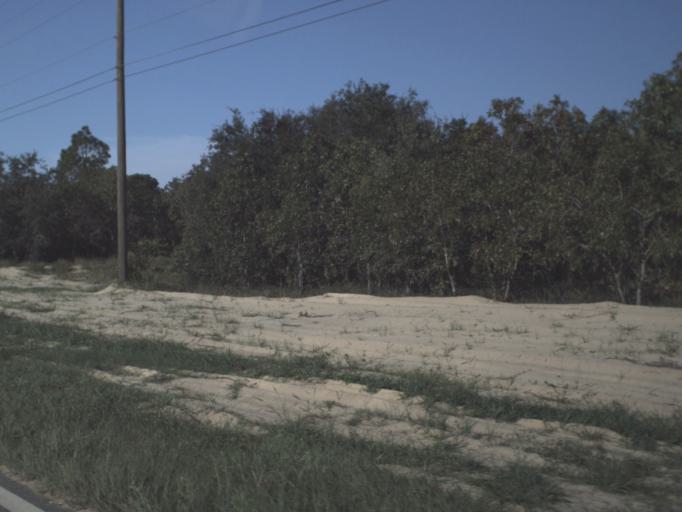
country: US
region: Florida
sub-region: Polk County
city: Davenport
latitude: 28.1987
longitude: -81.5827
